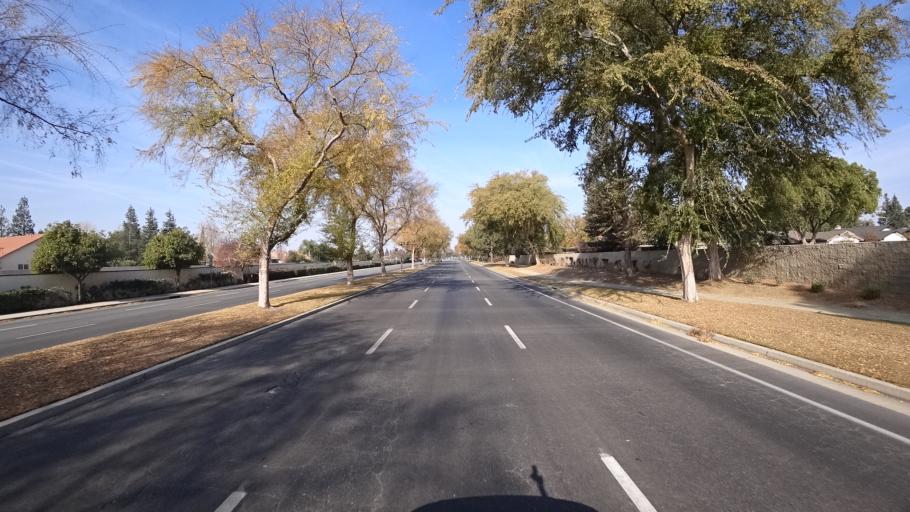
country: US
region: California
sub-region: Kern County
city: Greenacres
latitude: 35.3324
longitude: -119.1120
